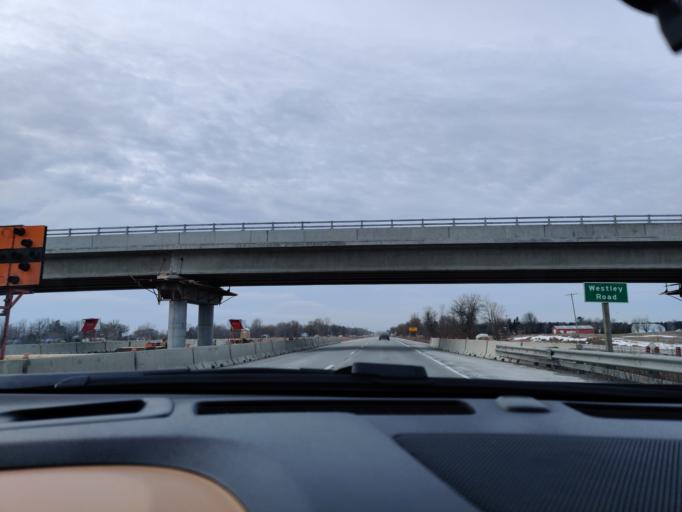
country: CA
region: Quebec
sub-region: Monteregie
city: Les Coteaux
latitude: 45.1629
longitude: -74.4438
